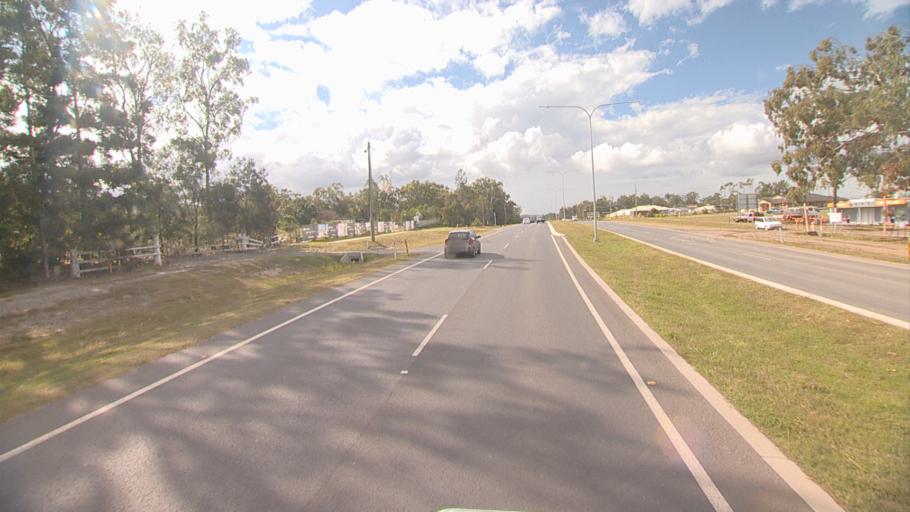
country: AU
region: Queensland
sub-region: Logan
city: Logan Reserve
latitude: -27.7060
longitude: 153.0946
